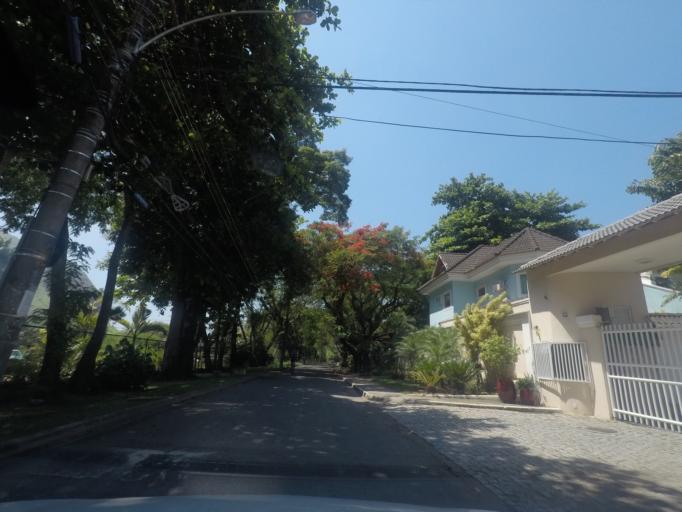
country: BR
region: Rio de Janeiro
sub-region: Nilopolis
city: Nilopolis
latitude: -22.9823
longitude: -43.4592
